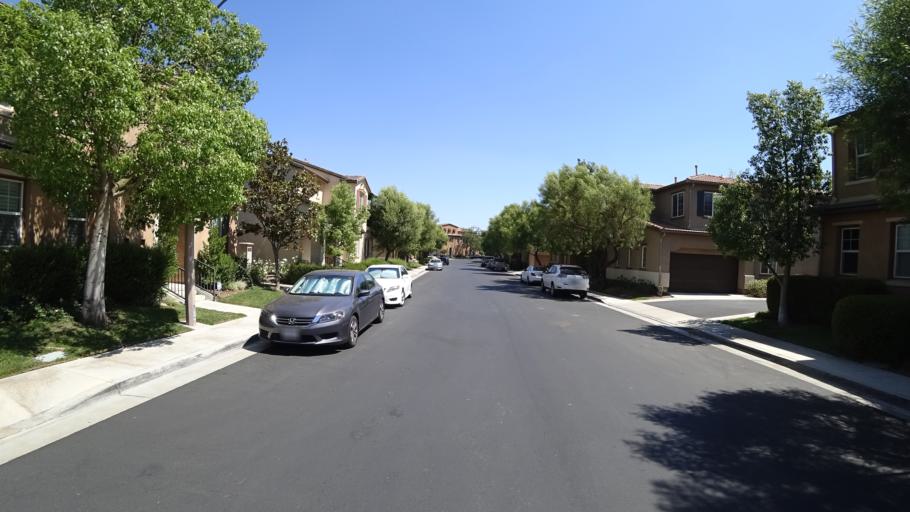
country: US
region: California
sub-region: Los Angeles County
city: Valencia
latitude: 34.4149
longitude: -118.5820
